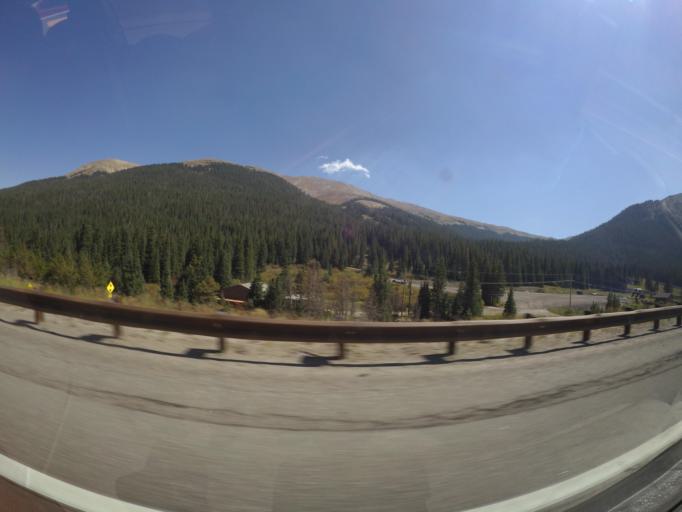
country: US
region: Colorado
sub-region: Summit County
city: Keystone
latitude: 39.6871
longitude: -105.8858
